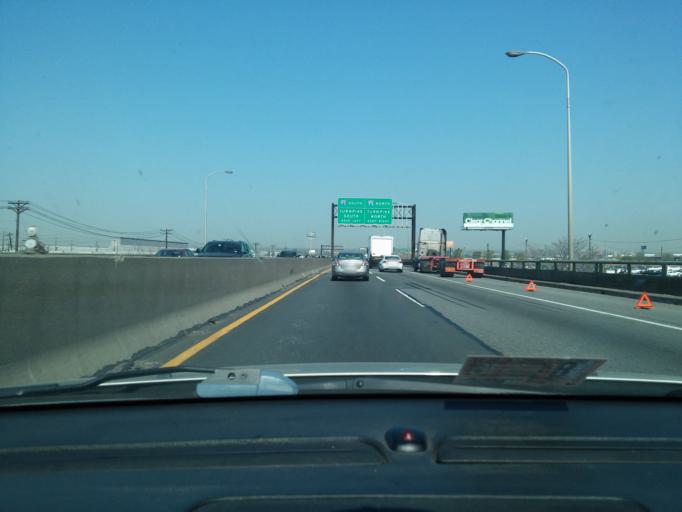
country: US
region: New Jersey
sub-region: Hudson County
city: Bayonne
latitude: 40.7017
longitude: -74.1389
